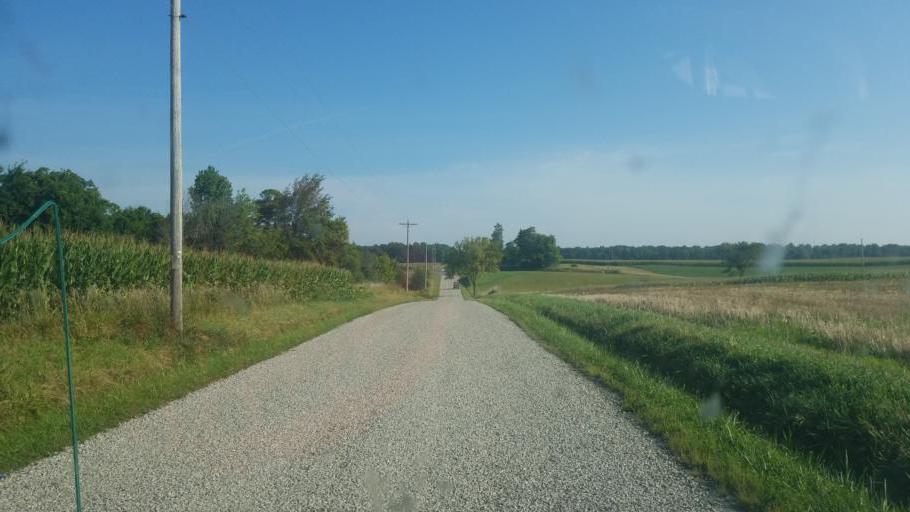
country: US
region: Ohio
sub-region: Ashland County
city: Ashland
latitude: 40.9557
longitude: -82.3399
